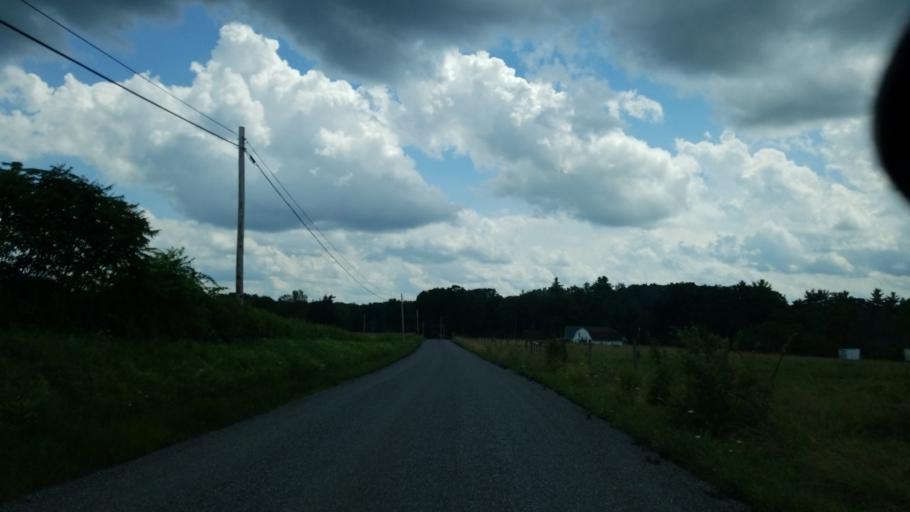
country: US
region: Pennsylvania
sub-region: Jefferson County
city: Brookville
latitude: 41.2347
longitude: -79.0116
